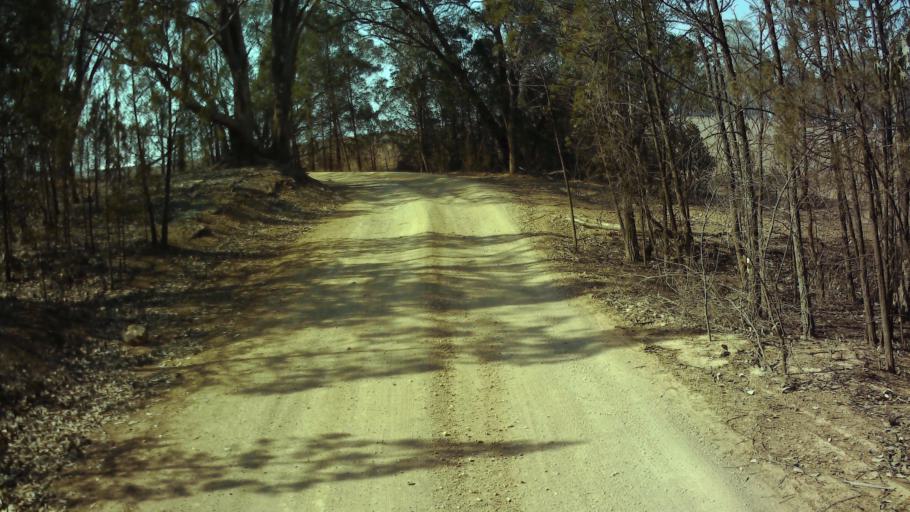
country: AU
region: New South Wales
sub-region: Weddin
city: Grenfell
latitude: -33.8954
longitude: 148.1786
